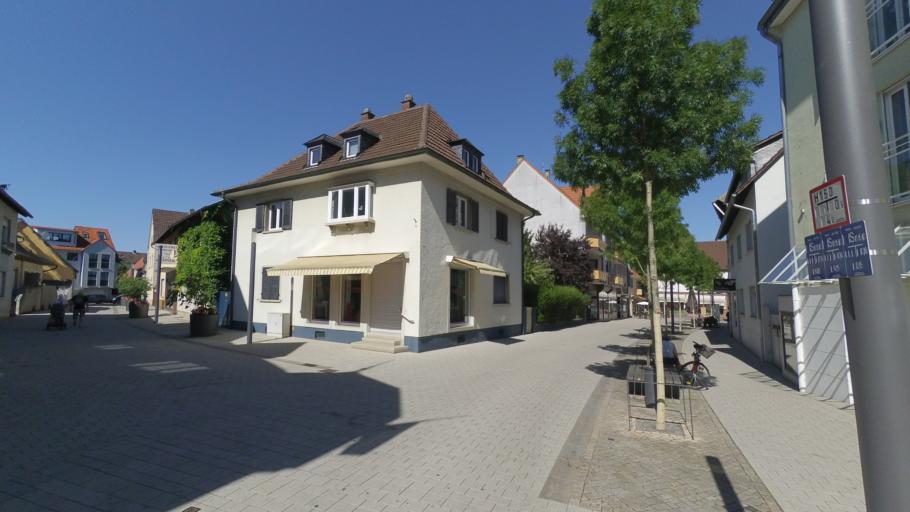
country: DE
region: Hesse
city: Viernheim
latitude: 49.5392
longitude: 8.5804
